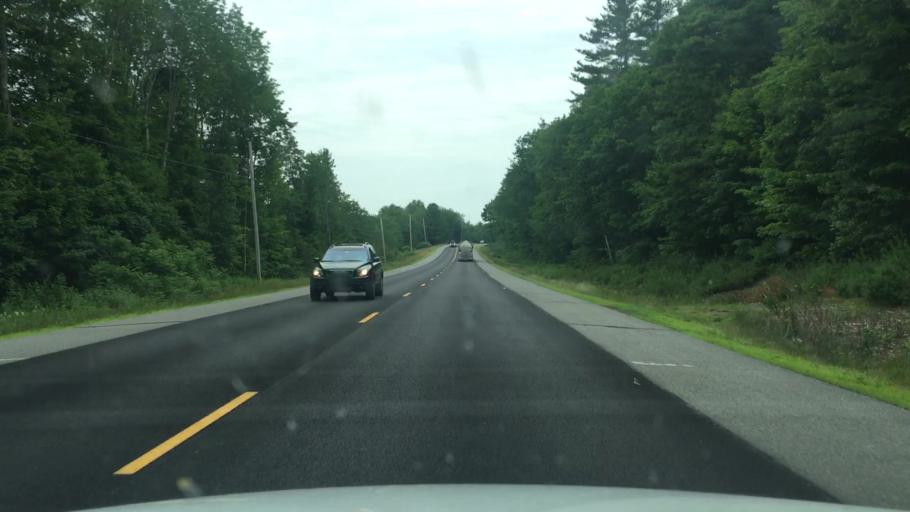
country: US
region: Maine
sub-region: Knox County
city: Washington
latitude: 44.3756
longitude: -69.3736
